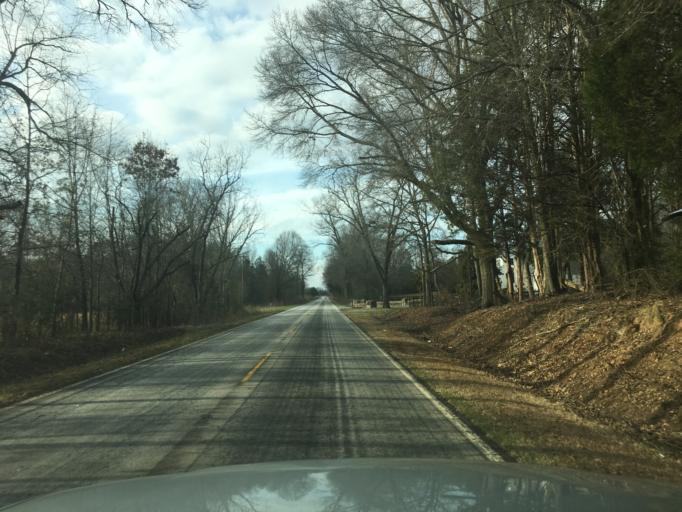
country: US
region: South Carolina
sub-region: Abbeville County
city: Lake Secession
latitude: 34.3506
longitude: -82.5014
